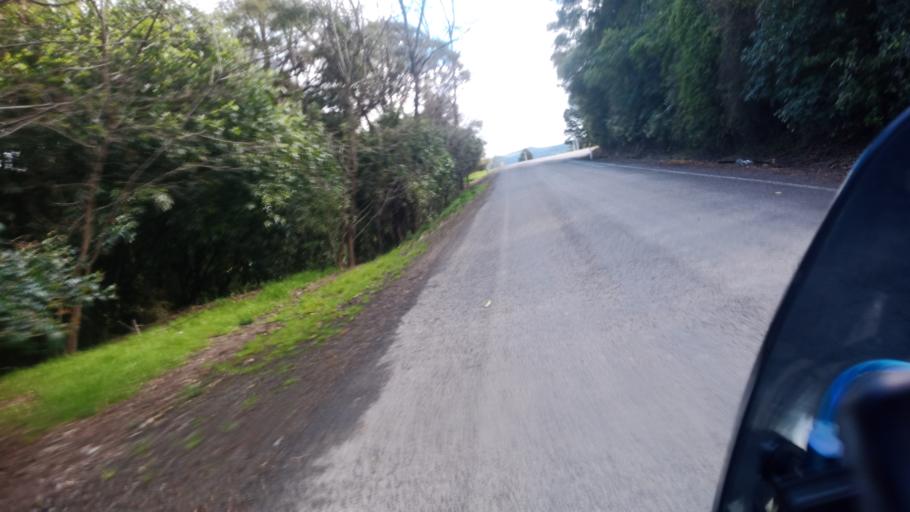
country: NZ
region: Gisborne
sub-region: Gisborne District
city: Gisborne
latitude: -38.3309
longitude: 178.2525
